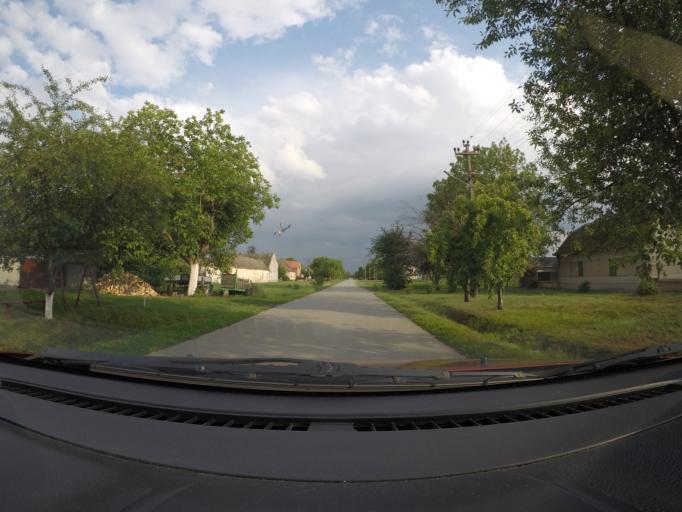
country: RS
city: Debeljaca
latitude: 45.0782
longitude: 20.5985
